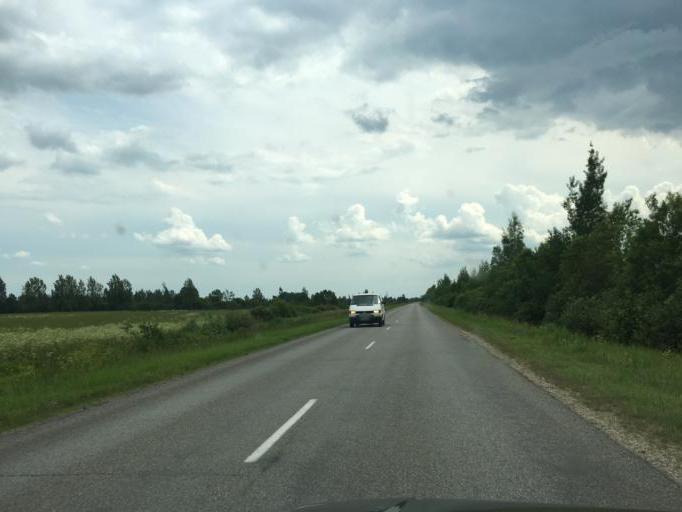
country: LV
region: Rugaju
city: Rugaji
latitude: 56.9280
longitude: 27.0685
